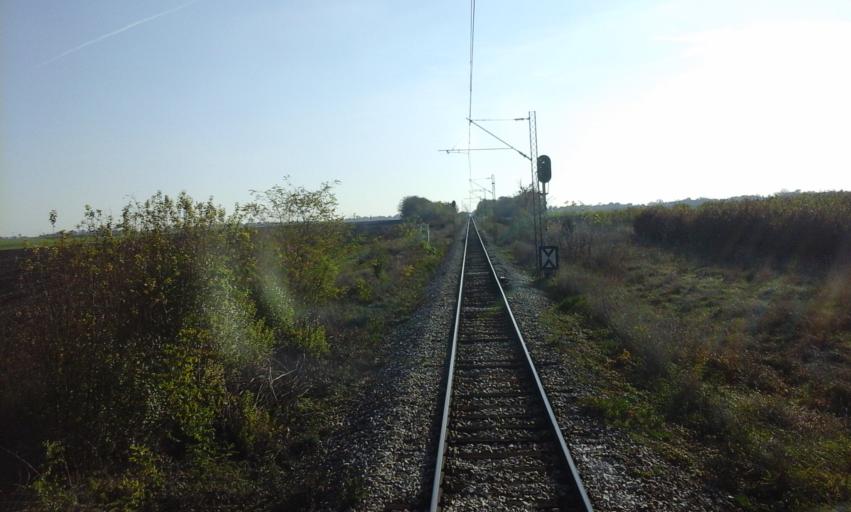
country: RS
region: Autonomna Pokrajina Vojvodina
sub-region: Severnobacki Okrug
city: Backa Topola
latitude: 45.7652
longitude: 19.6483
